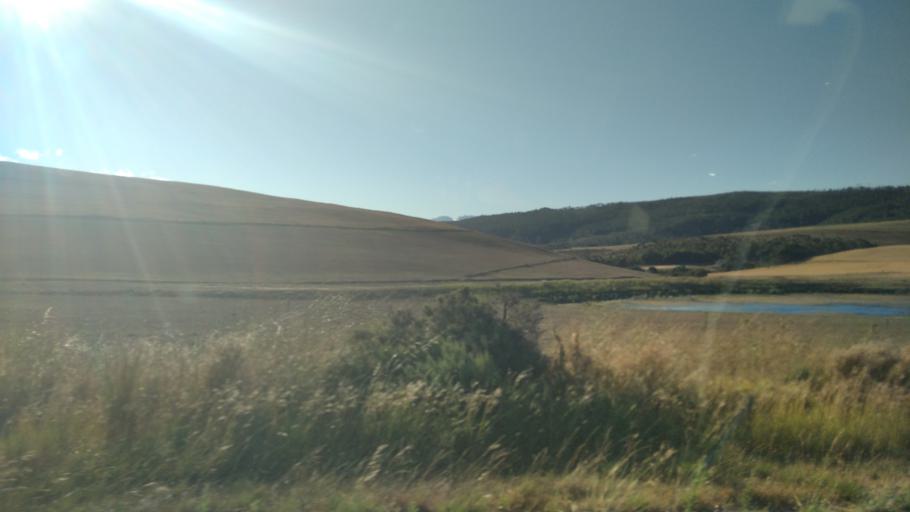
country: ZA
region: Western Cape
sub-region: Overberg District Municipality
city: Caledon
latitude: -34.1212
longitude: 19.2989
